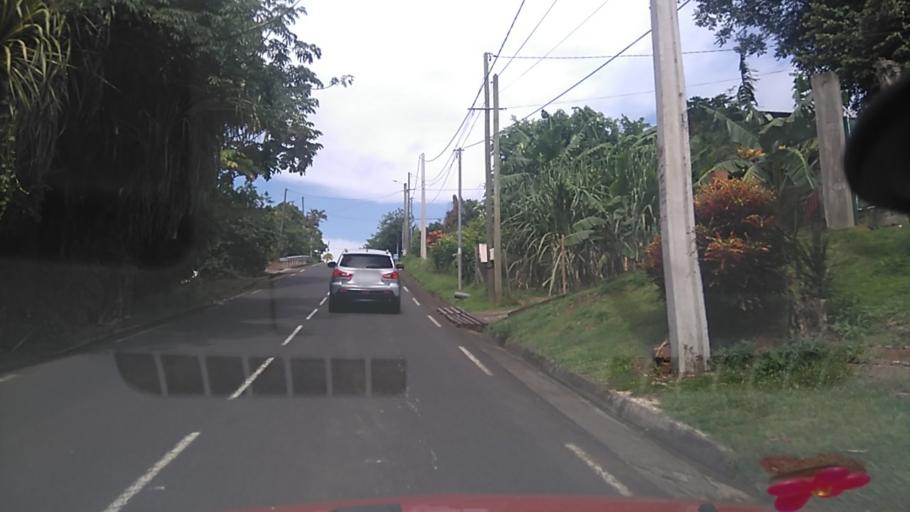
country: MQ
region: Martinique
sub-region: Martinique
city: Le Francois
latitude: 14.5941
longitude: -60.9230
